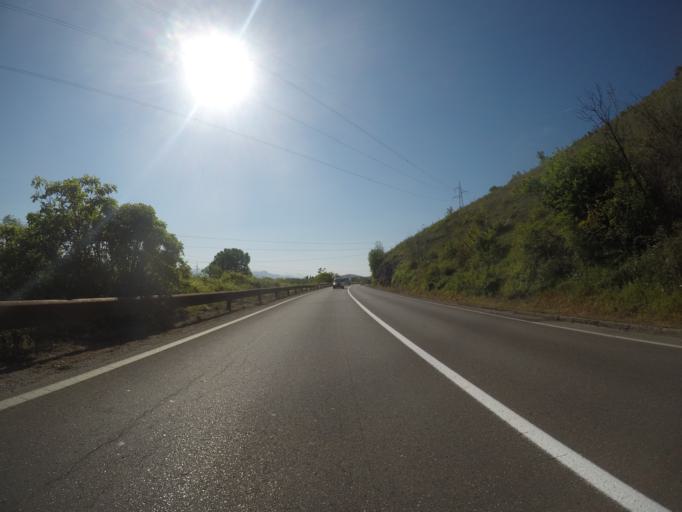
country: ME
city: Spuz
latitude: 42.4495
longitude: 19.2000
